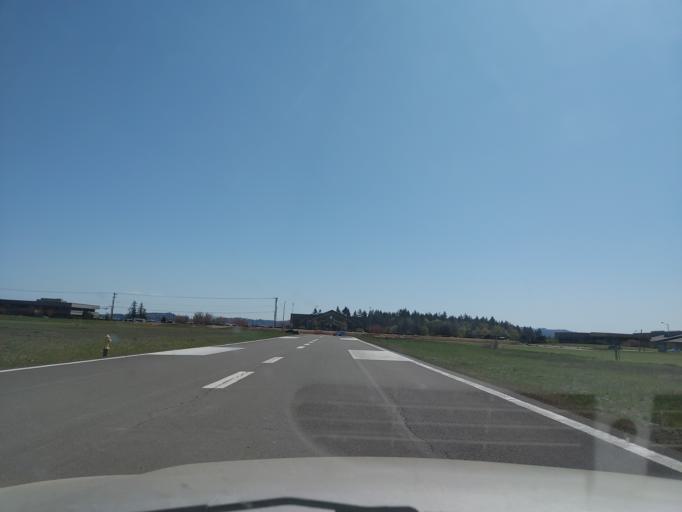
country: US
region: Oregon
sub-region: Yamhill County
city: Lafayette
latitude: 45.2028
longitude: -123.1455
